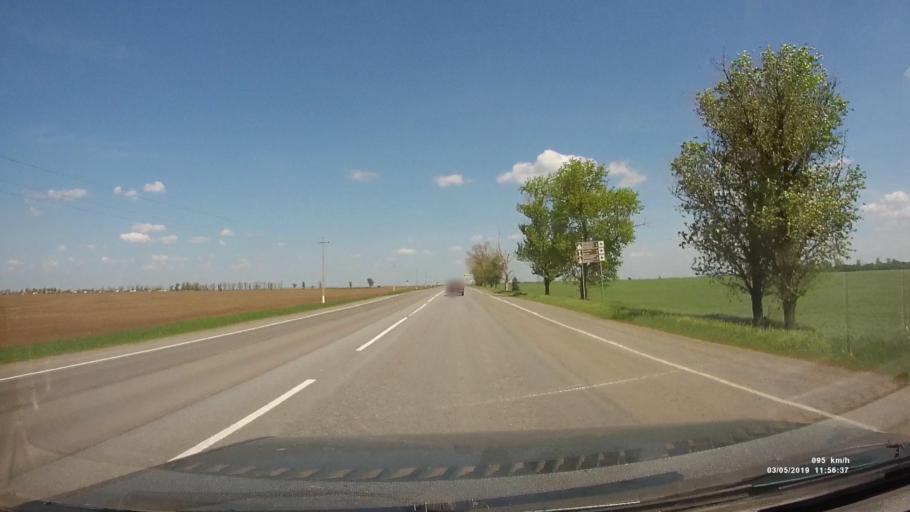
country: RU
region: Rostov
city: Bagayevskaya
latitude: 47.1971
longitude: 40.3028
